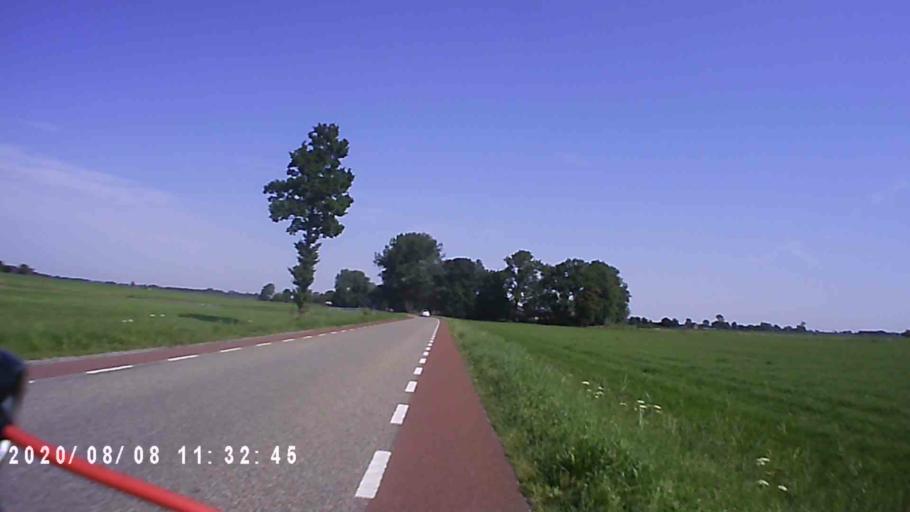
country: NL
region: Groningen
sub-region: Gemeente Zuidhorn
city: Zuidhorn
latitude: 53.2101
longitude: 6.3890
